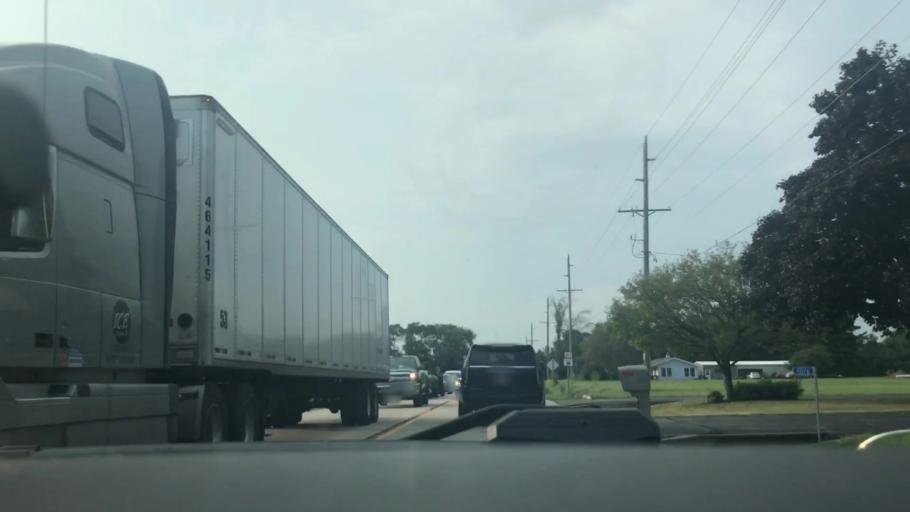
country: US
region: Wisconsin
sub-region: Washington County
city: Slinger
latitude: 43.3756
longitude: -88.3390
